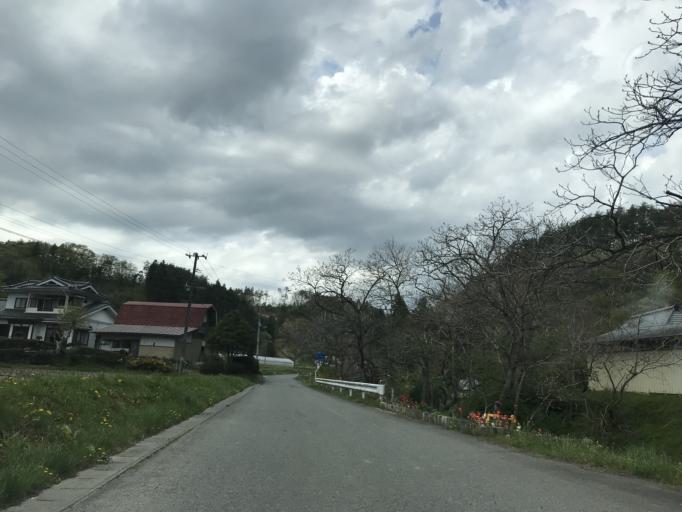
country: JP
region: Iwate
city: Ichinoseki
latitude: 38.7918
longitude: 141.4225
